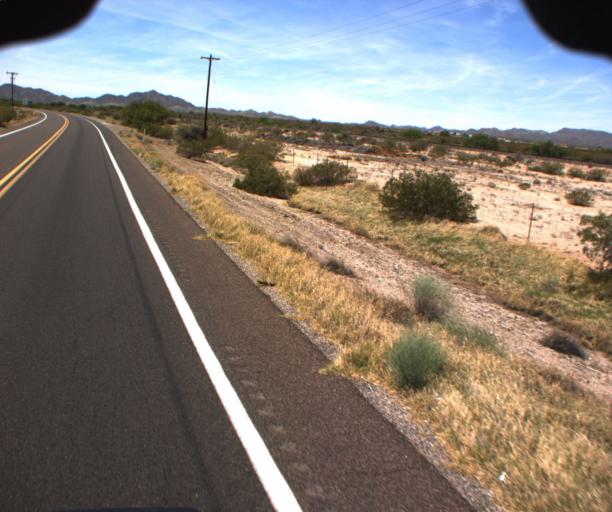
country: US
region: Arizona
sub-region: La Paz County
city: Salome
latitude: 33.7779
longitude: -113.6207
